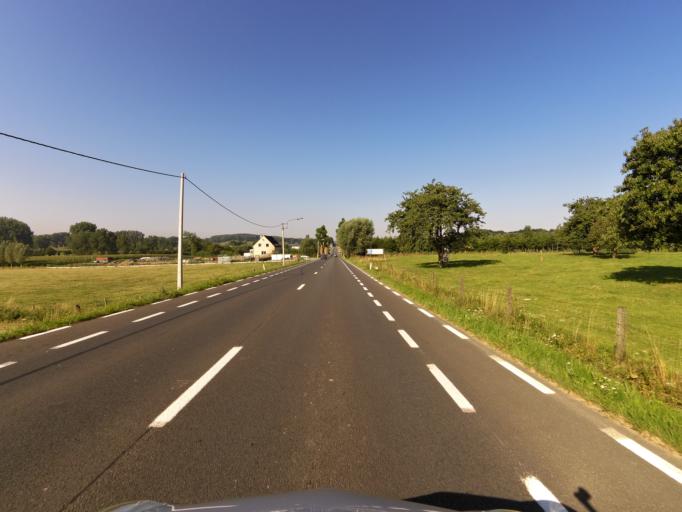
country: BE
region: Flanders
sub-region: Provincie Oost-Vlaanderen
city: Sint-Maria-Lierde
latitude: 50.8119
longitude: 3.8036
